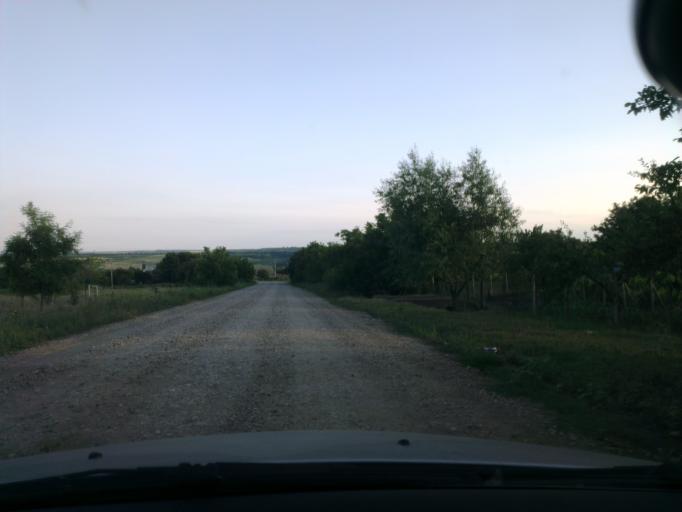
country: MD
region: Cantemir
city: Visniovca
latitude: 46.3368
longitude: 28.4026
